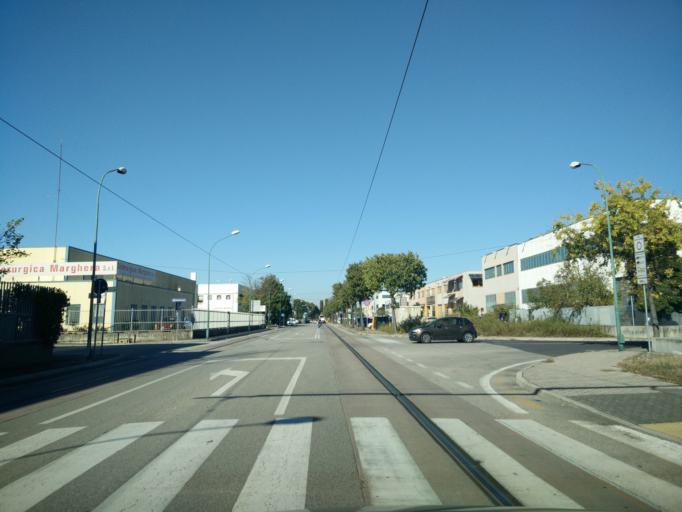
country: IT
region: Veneto
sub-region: Provincia di Venezia
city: Mestre
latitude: 45.4633
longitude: 12.2166
